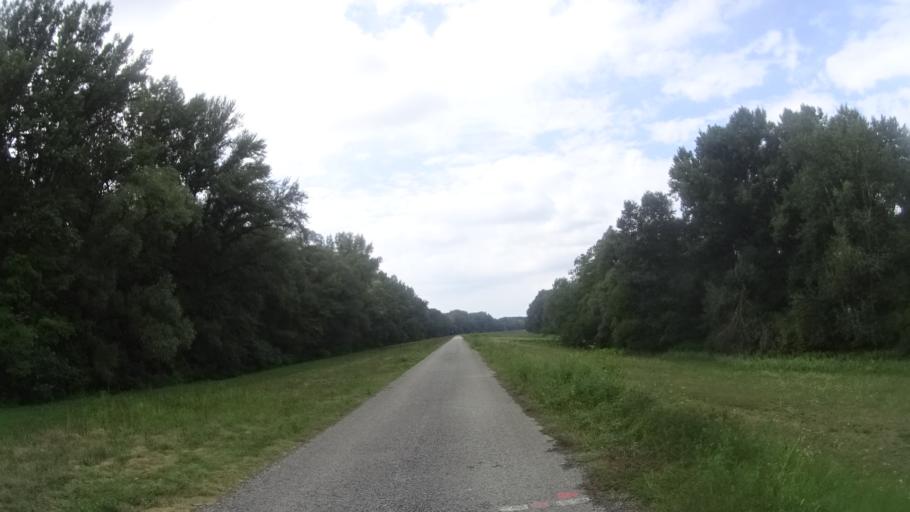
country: SK
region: Trnavsky
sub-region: Okres Dunajska Streda
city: Velky Meder
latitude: 47.7668
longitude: 17.7241
